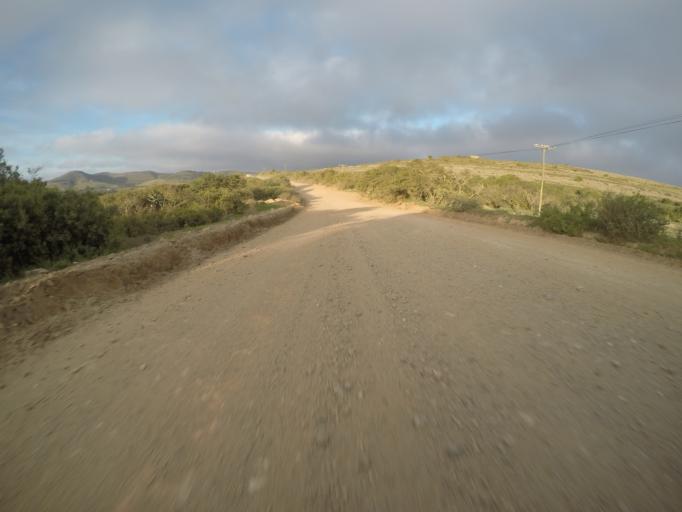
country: ZA
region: Western Cape
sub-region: Eden District Municipality
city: Mossel Bay
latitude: -34.1100
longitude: 22.0597
